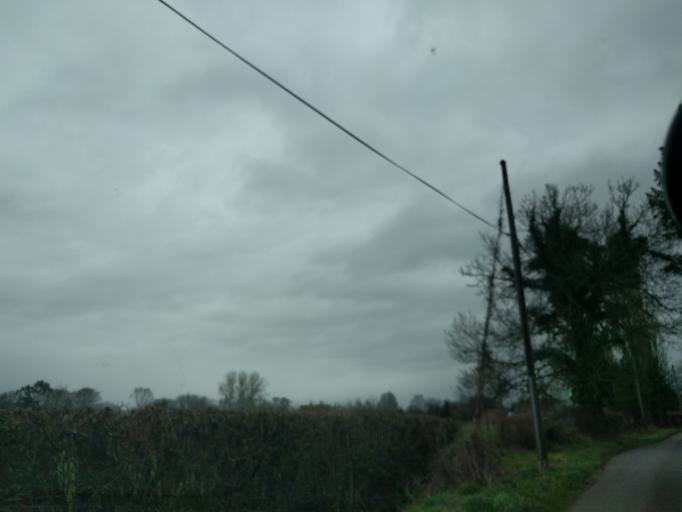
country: GB
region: England
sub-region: Gloucestershire
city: Dursley
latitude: 51.7093
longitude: -2.3235
